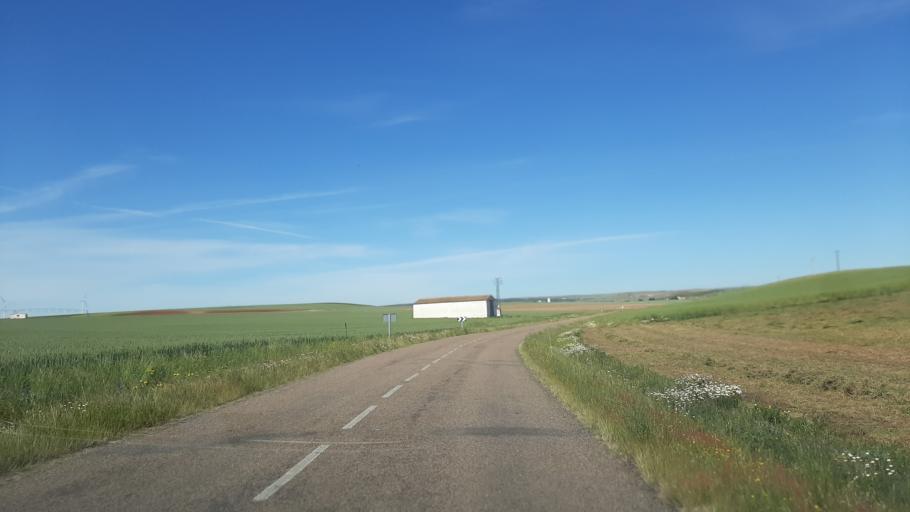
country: ES
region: Castille and Leon
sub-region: Provincia de Salamanca
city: Aldeaseca de Alba
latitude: 40.8172
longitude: -5.4635
